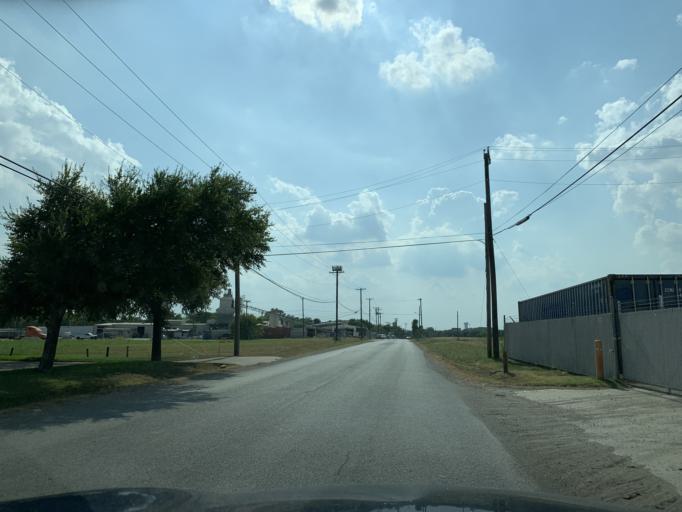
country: US
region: Texas
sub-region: Tarrant County
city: Richland Hills
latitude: 32.7946
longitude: -97.2283
